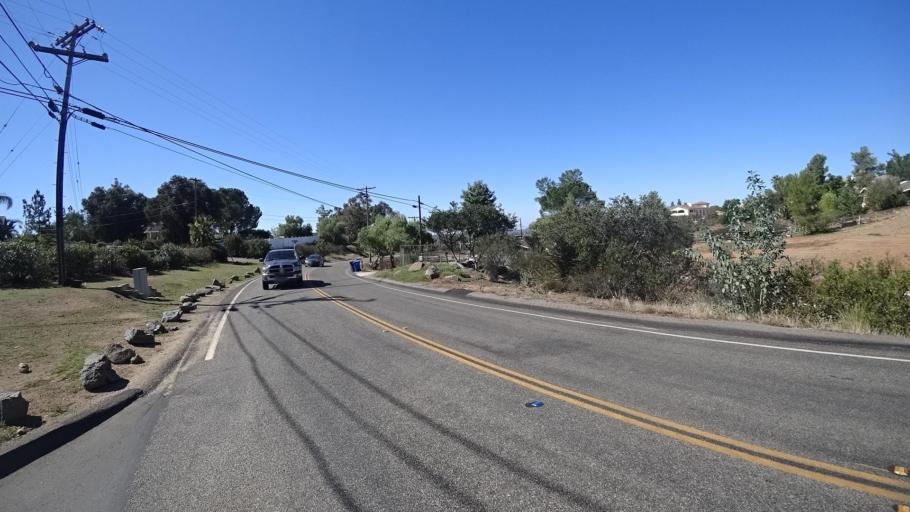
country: US
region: California
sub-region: San Diego County
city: Alpine
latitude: 32.8378
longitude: -116.7483
